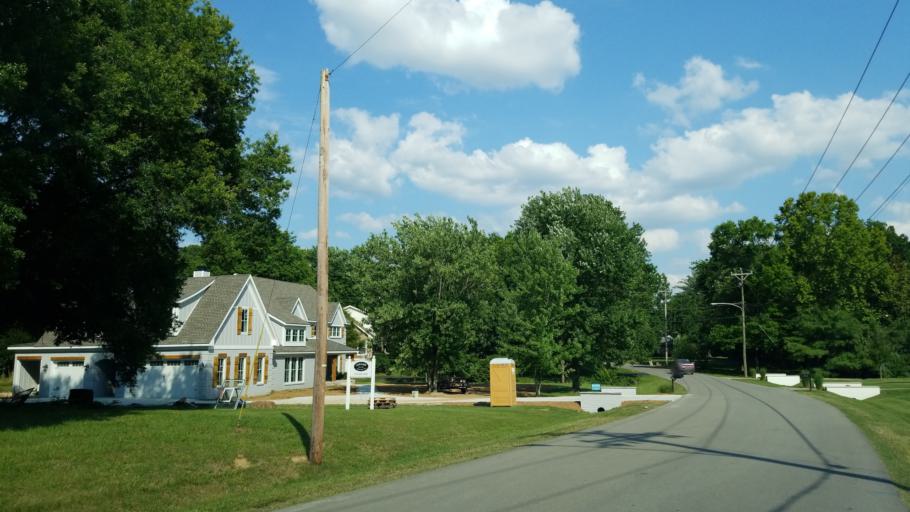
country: US
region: Tennessee
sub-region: Davidson County
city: Forest Hills
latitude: 36.0385
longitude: -86.8306
